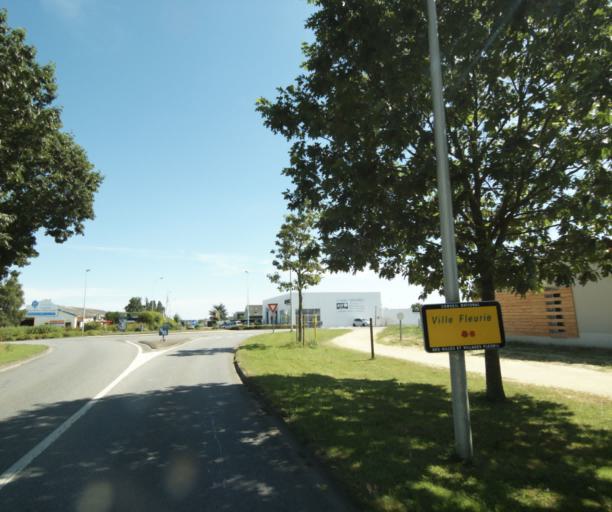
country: FR
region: Pays de la Loire
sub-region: Departement de la Mayenne
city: Laval
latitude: 48.0302
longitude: -0.7746
